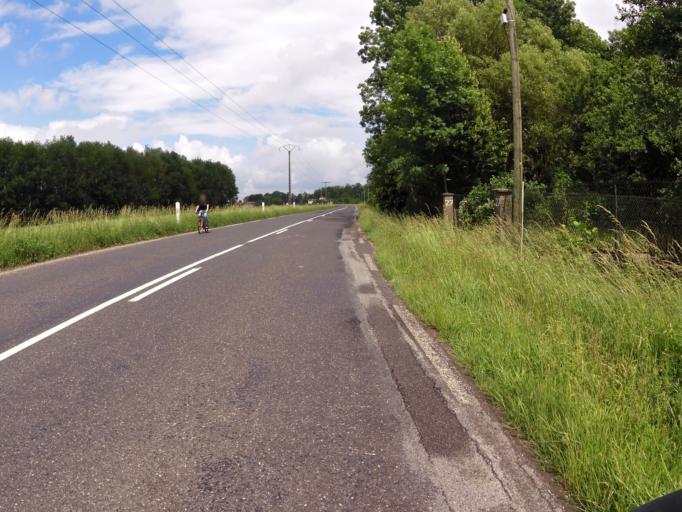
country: FR
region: Lorraine
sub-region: Departement de la Meuse
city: Revigny-sur-Ornain
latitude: 48.8128
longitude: 4.9705
